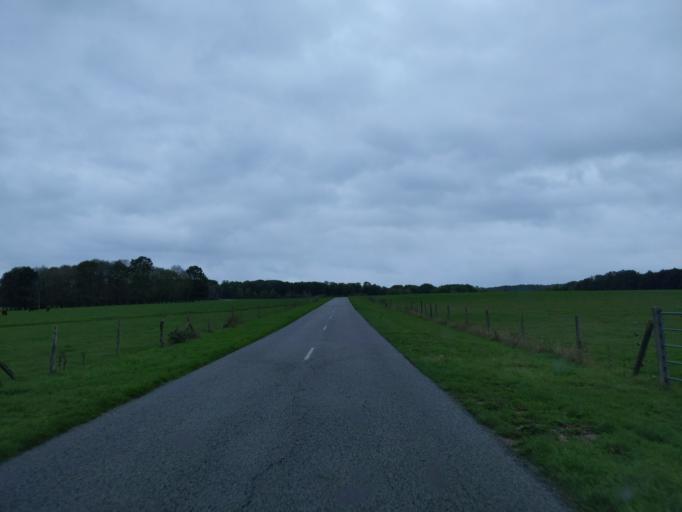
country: FR
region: Ile-de-France
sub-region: Departement des Yvelines
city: Bullion
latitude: 48.6254
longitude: 1.9827
